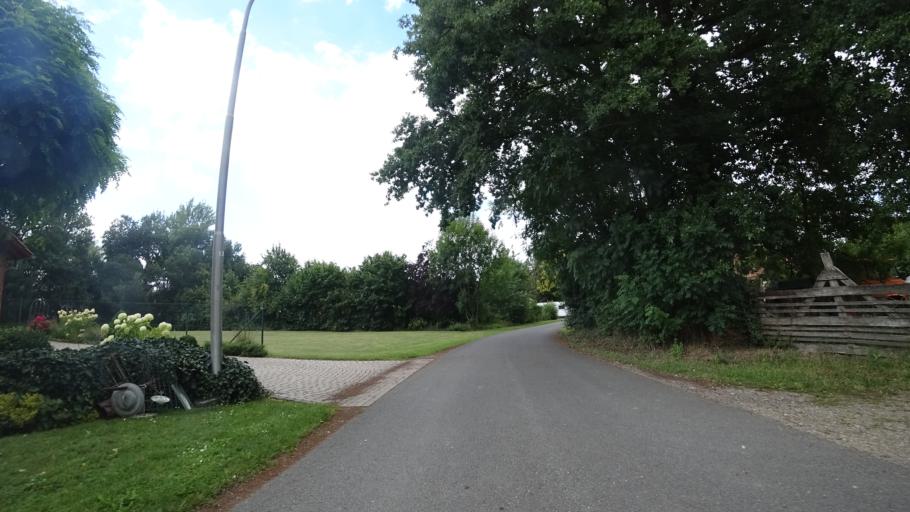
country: DE
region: Lower Saxony
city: Raddestorf
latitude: 52.4579
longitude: 9.0230
